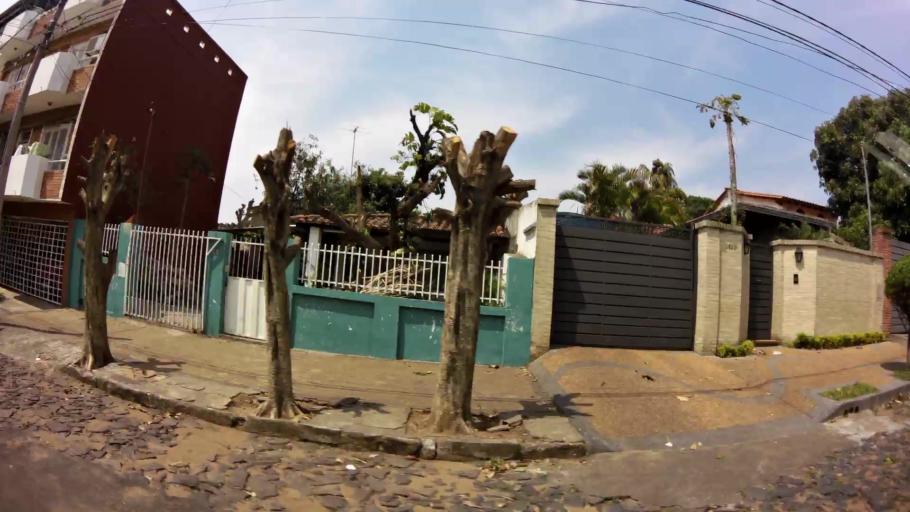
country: PY
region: Asuncion
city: Asuncion
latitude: -25.2739
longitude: -57.6007
